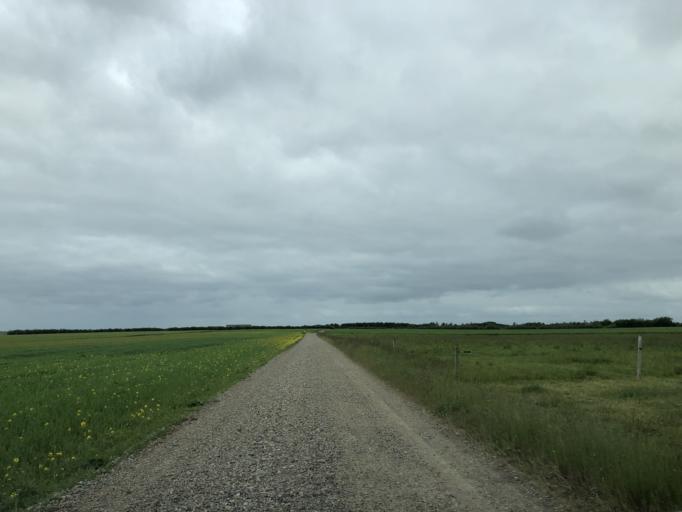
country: DK
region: Central Jutland
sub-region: Holstebro Kommune
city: Ulfborg
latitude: 56.2274
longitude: 8.1857
